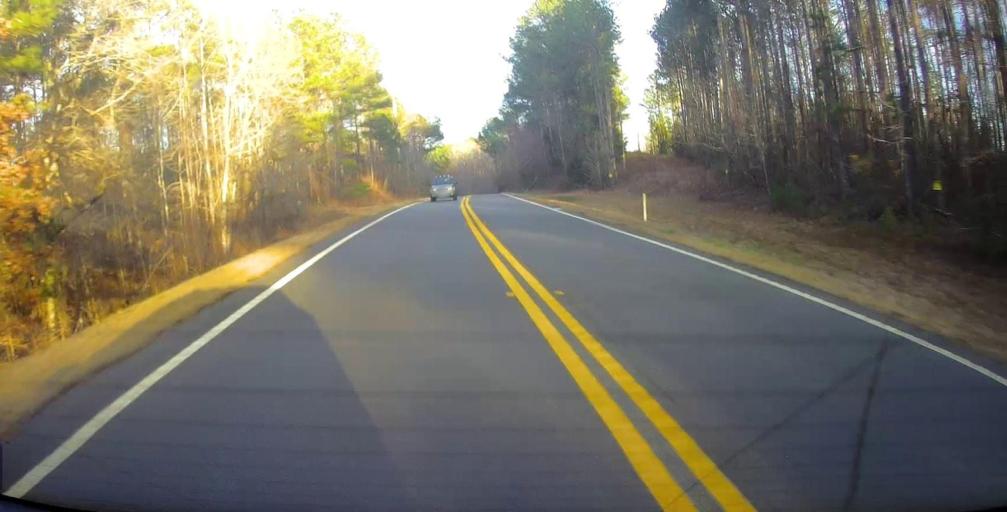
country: US
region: Georgia
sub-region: Talbot County
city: Sardis
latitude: 32.7231
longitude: -84.6445
